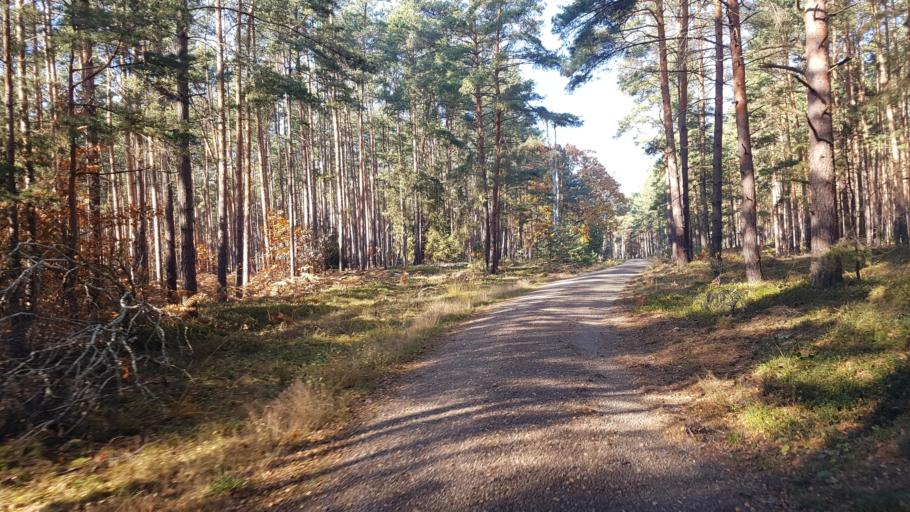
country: DE
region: Brandenburg
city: Ruckersdorf
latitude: 51.5664
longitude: 13.6186
